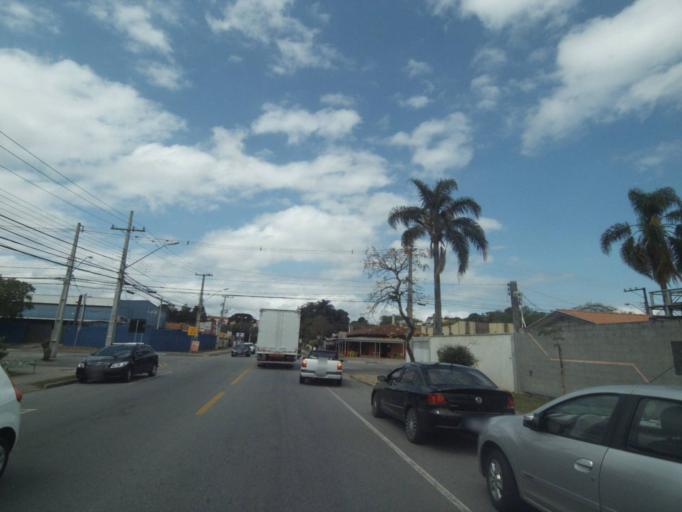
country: BR
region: Parana
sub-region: Pinhais
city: Pinhais
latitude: -25.4143
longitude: -49.2192
